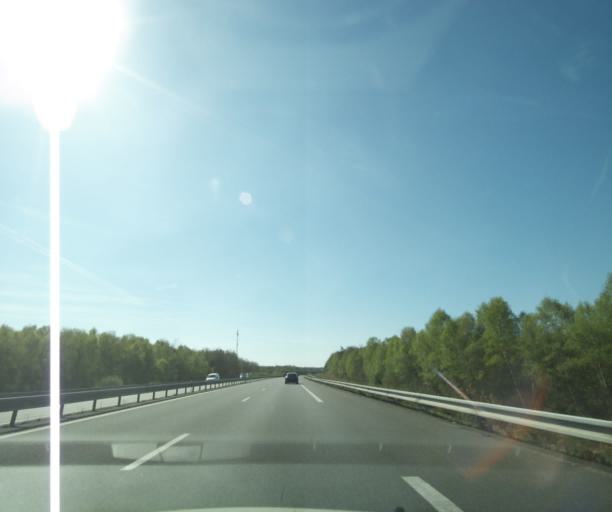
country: FR
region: Centre
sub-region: Departement du Loir-et-Cher
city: Salbris
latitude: 47.3777
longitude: 2.0526
